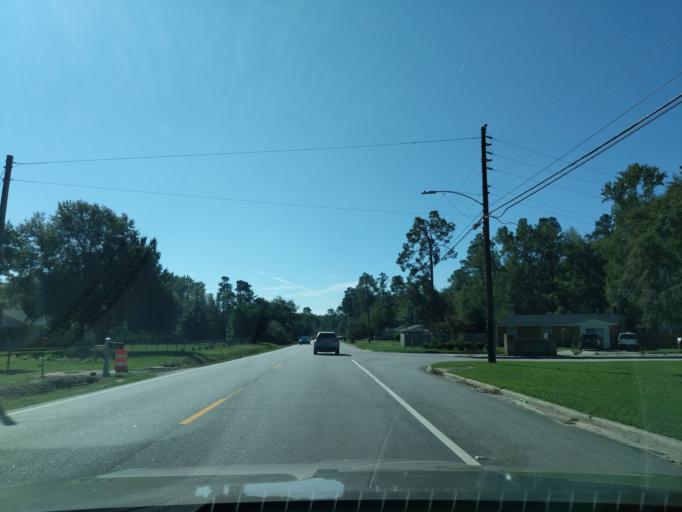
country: US
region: Georgia
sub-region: Richmond County
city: Hephzibah
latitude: 33.3607
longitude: -81.9972
